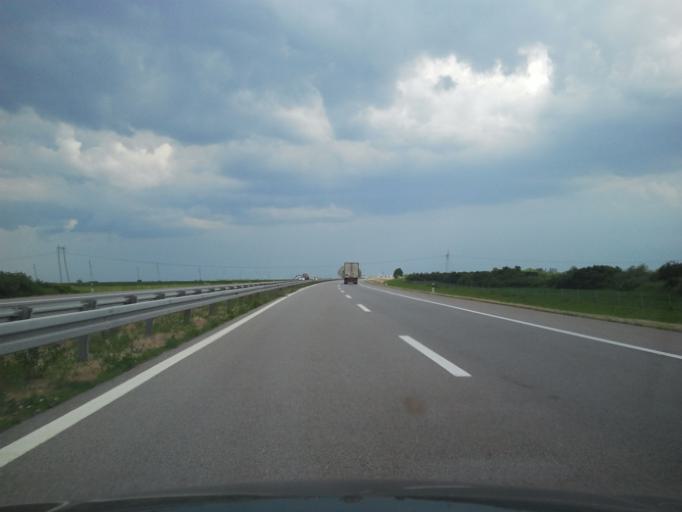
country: RS
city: Ravnje
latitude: 45.0419
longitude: 19.4307
